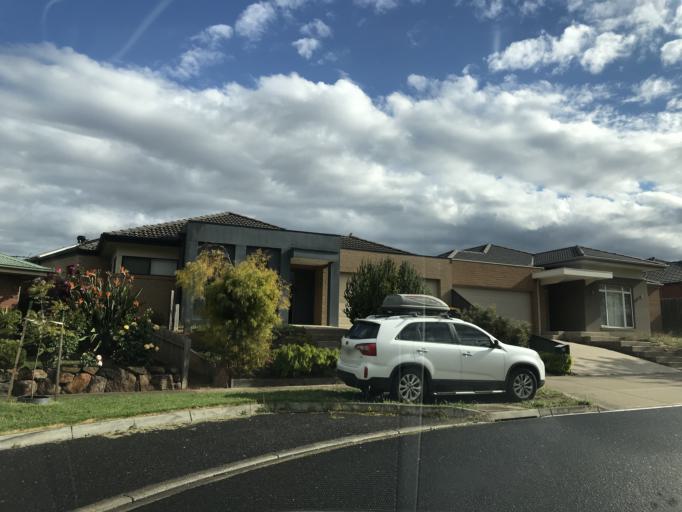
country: AU
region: Victoria
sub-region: Brimbank
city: Derrimut
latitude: -37.7882
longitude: 144.7697
